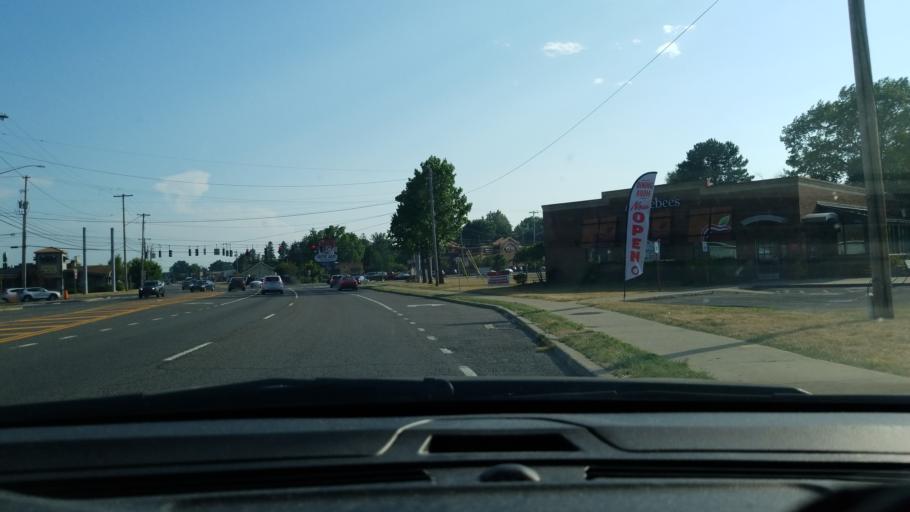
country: US
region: New York
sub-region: Onondaga County
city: North Syracuse
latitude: 43.1236
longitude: -76.1413
